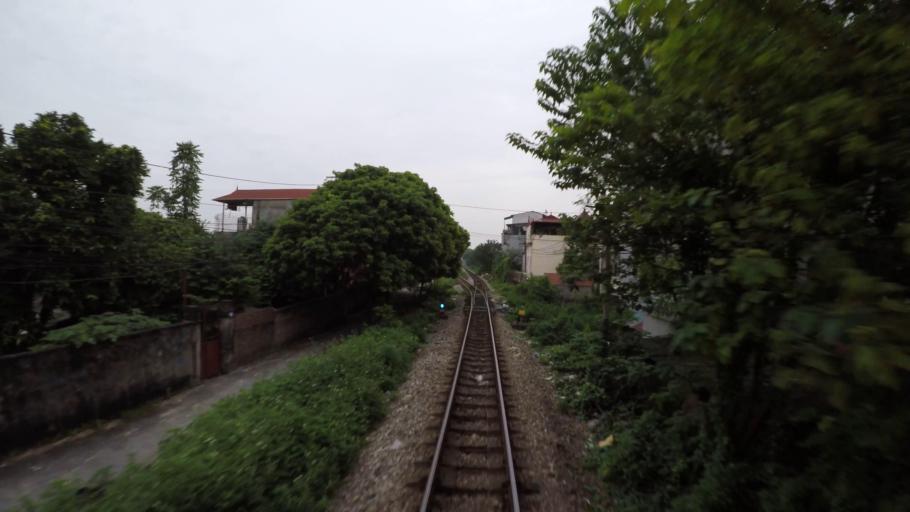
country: VN
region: Ha Noi
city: Trau Quy
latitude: 21.0380
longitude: 105.8984
